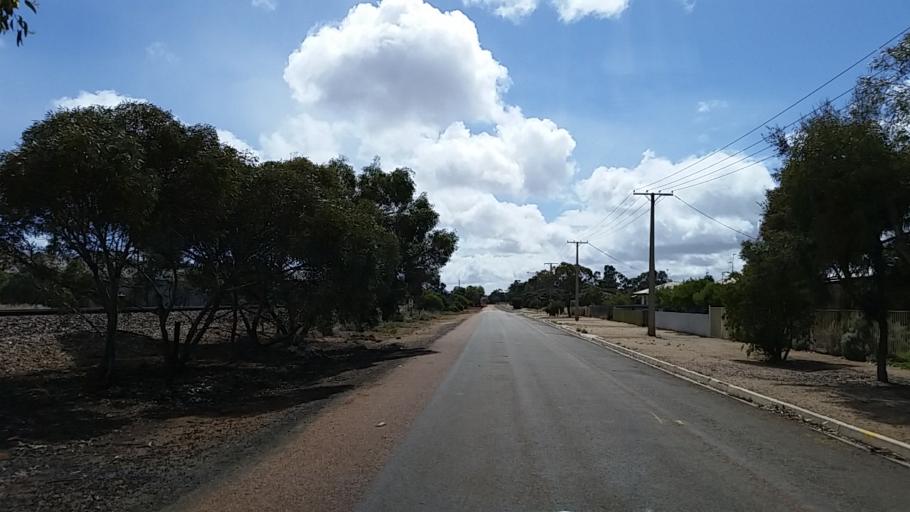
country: AU
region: South Australia
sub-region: Peterborough
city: Peterborough
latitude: -32.9771
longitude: 138.8242
